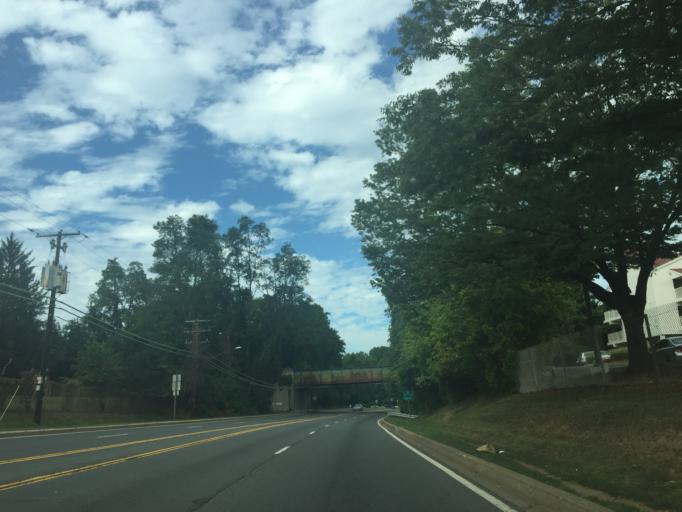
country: US
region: Maryland
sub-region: Montgomery County
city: Gaithersburg
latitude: 39.1460
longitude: -77.2196
